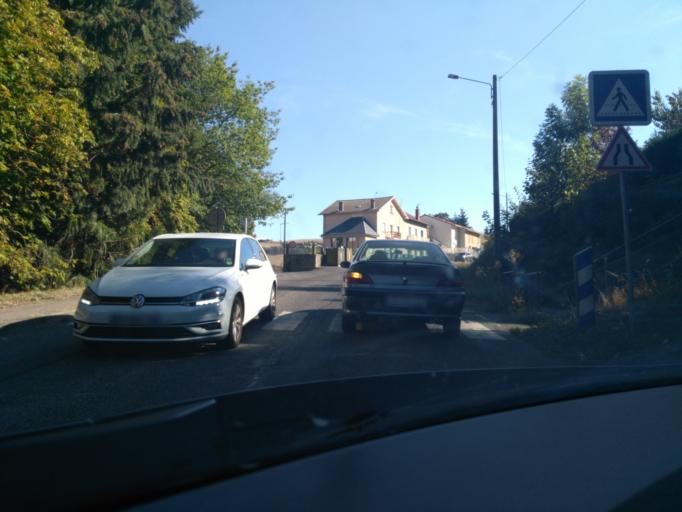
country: FR
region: Rhone-Alpes
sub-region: Departement du Rhone
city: Tarare
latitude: 45.8909
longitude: 4.4341
